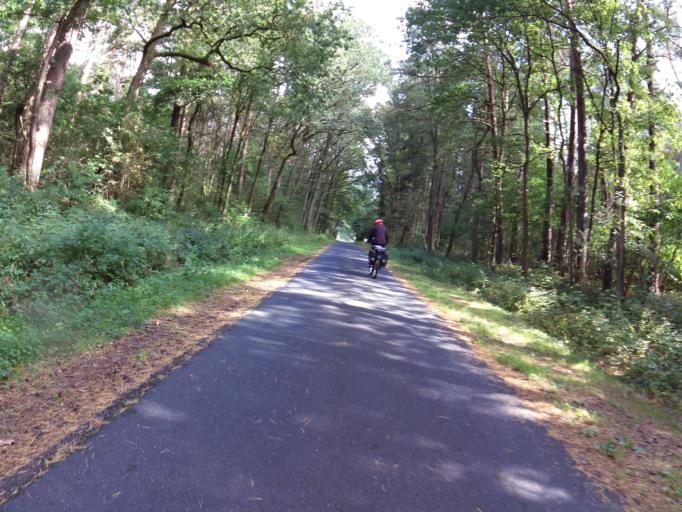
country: DE
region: Lower Saxony
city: Seedorf
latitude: 53.3255
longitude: 9.2290
